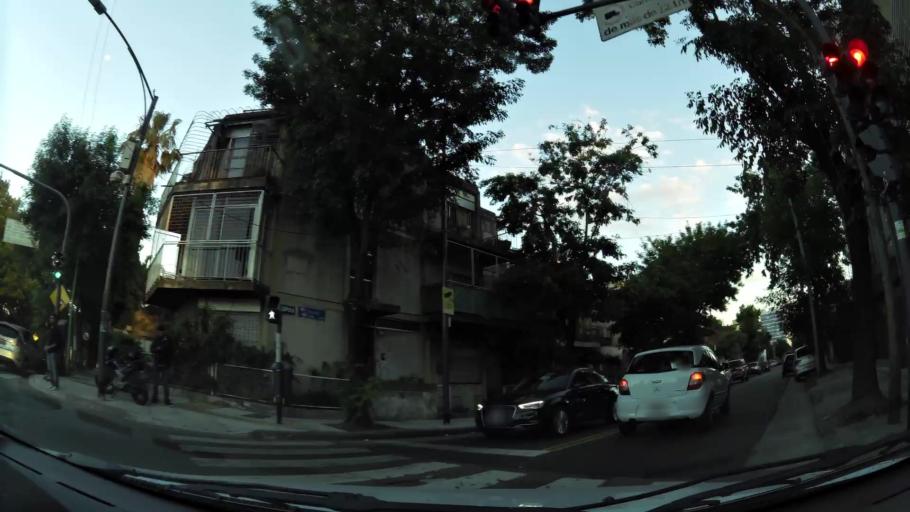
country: AR
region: Buenos Aires
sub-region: Partido de Vicente Lopez
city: Olivos
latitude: -34.5418
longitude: -58.4803
